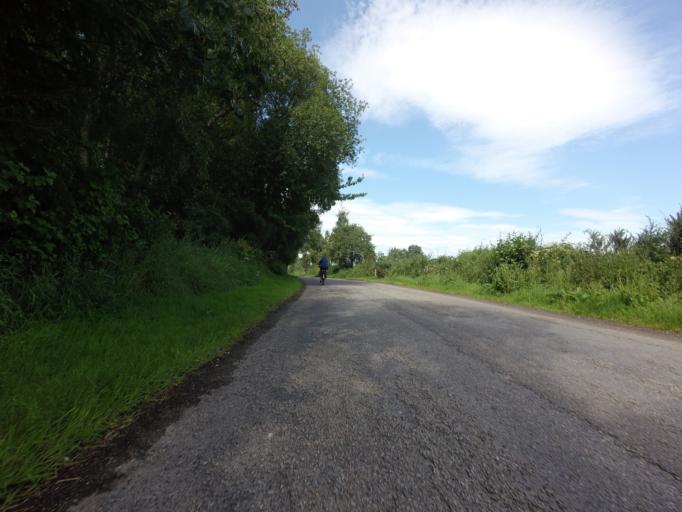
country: GB
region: Scotland
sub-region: Highland
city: Inverness
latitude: 57.5180
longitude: -4.2910
